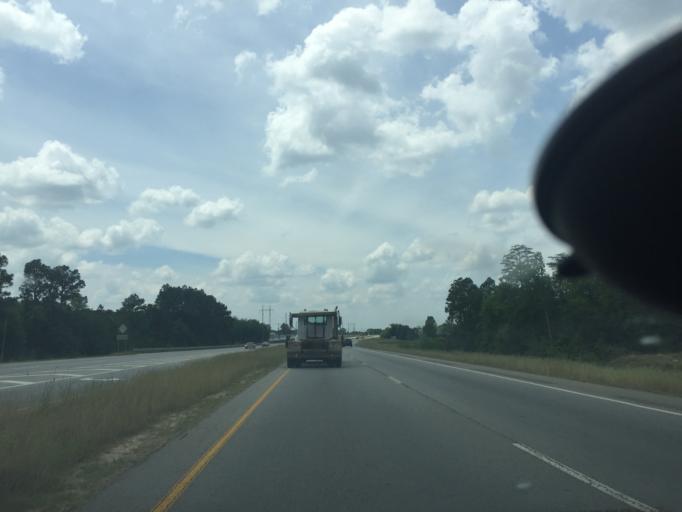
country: US
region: Georgia
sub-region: Bulloch County
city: Statesboro
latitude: 32.4059
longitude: -81.7711
